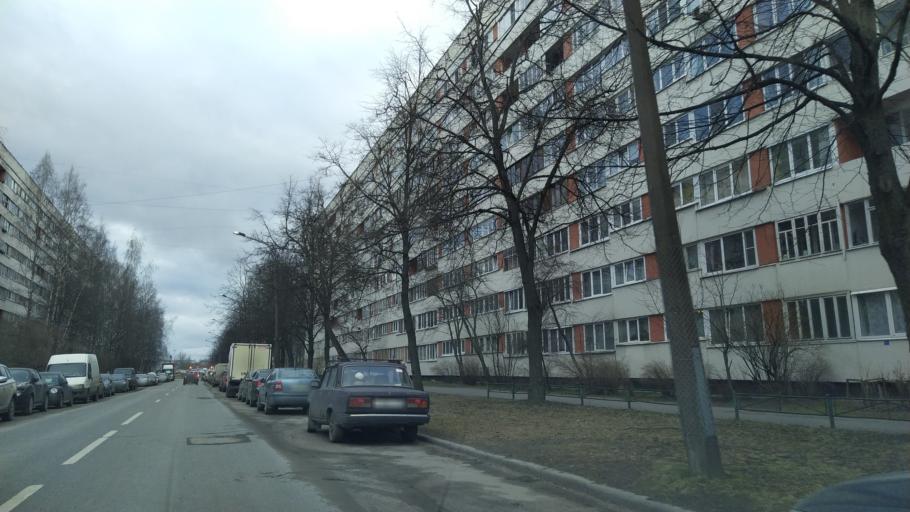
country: RU
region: Leningrad
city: Parnas
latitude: 60.0511
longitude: 30.3704
